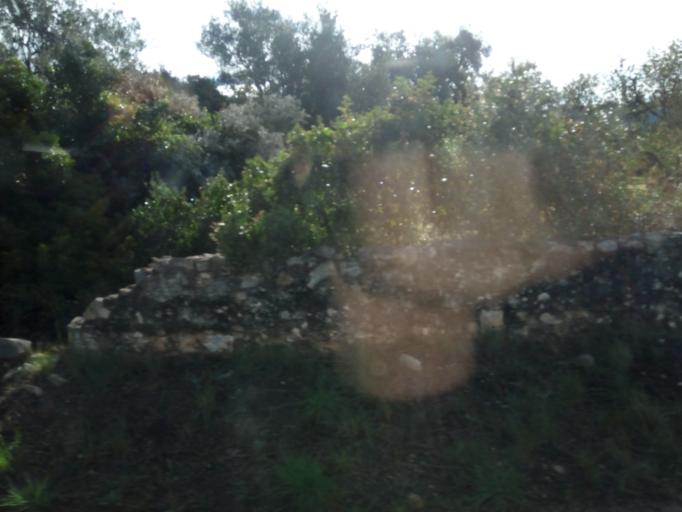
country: PT
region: Faro
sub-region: Faro
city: Santa Barbara de Nexe
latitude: 37.1299
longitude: -7.9766
